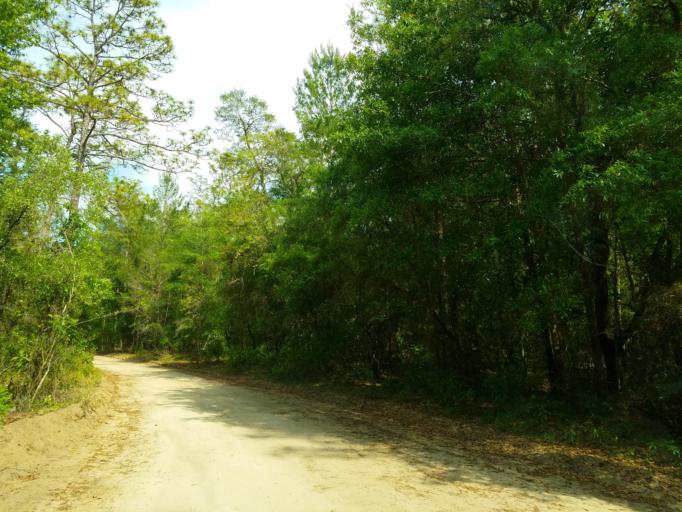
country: US
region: Florida
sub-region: Hernando County
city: Hill 'n Dale
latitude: 28.5502
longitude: -82.2799
